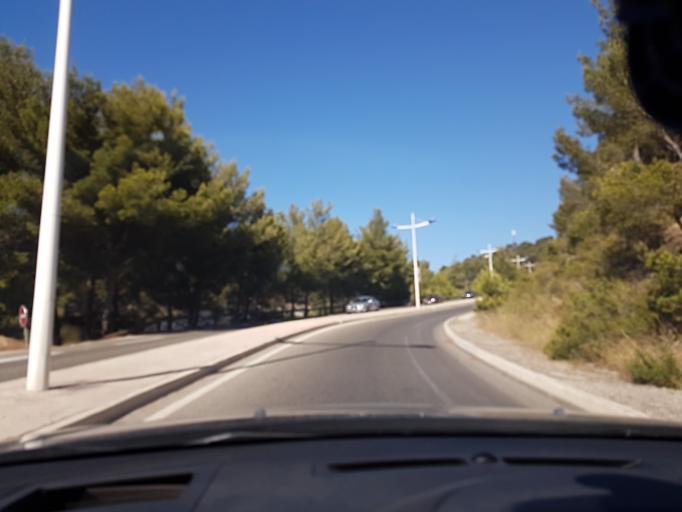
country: FR
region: Provence-Alpes-Cote d'Azur
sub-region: Departement des Bouches-du-Rhone
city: Carry-le-Rouet
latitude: 43.3379
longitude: 5.1590
